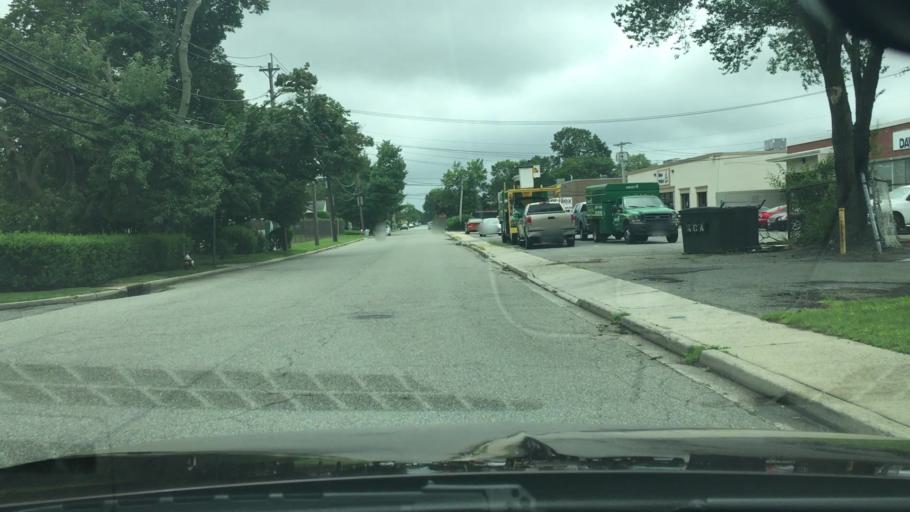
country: US
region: New York
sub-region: Nassau County
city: Hicksville
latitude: 40.7862
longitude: -73.5152
